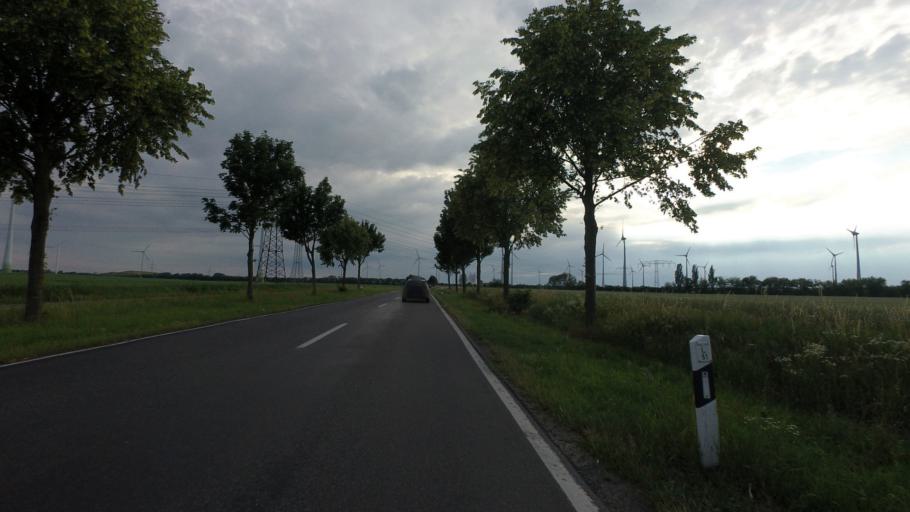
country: DE
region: Brandenburg
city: Nauen
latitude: 52.5964
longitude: 12.8268
